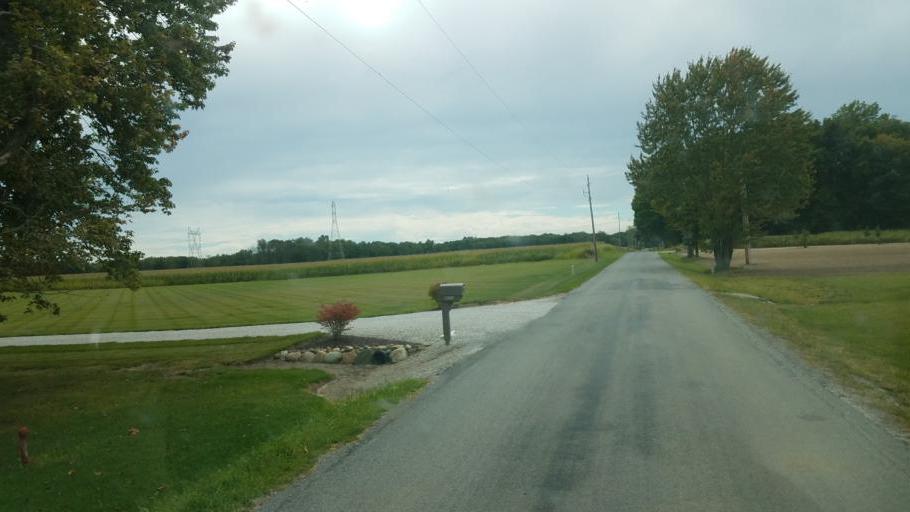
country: US
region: Ohio
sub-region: Delaware County
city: Sunbury
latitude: 40.2714
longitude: -82.7993
